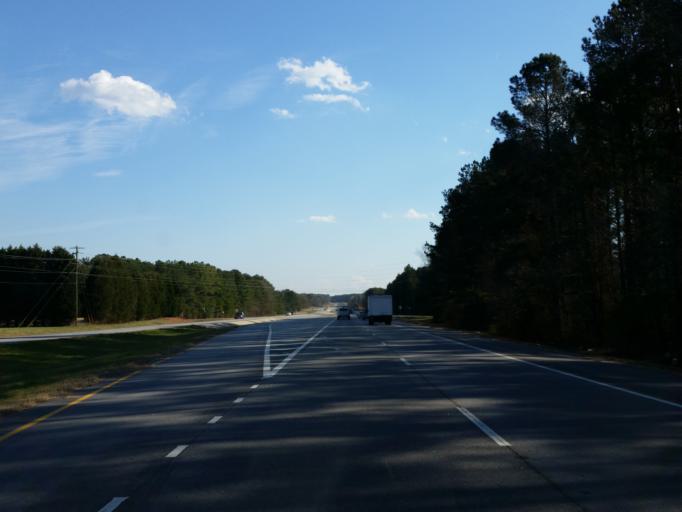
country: US
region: Georgia
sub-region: Spalding County
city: Griffin
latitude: 33.1686
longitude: -84.2612
